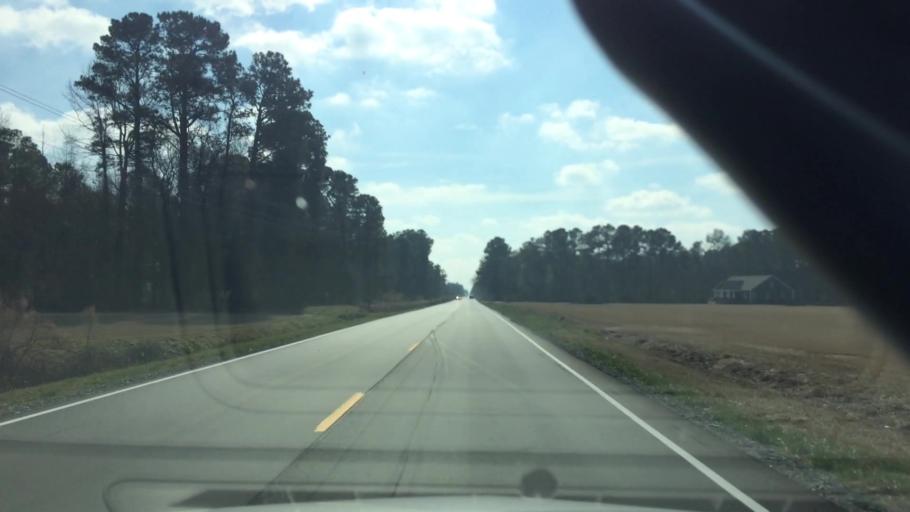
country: US
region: North Carolina
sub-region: Duplin County
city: Beulaville
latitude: 35.0272
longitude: -77.7487
